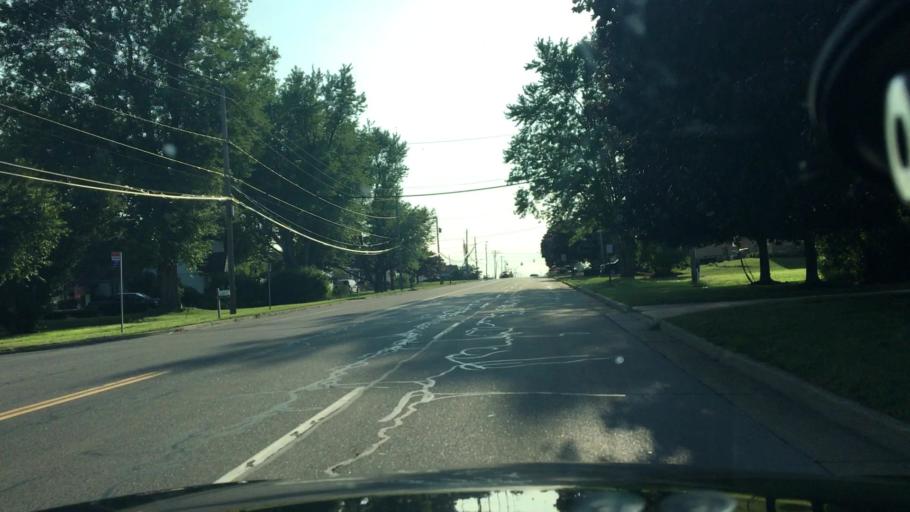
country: US
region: New York
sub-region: Erie County
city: Blasdell
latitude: 42.7969
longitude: -78.8073
